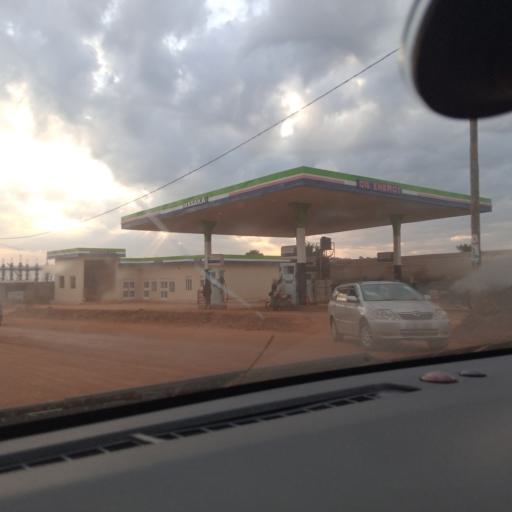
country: UG
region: Central Region
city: Masaka
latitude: -0.3367
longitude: 31.7400
